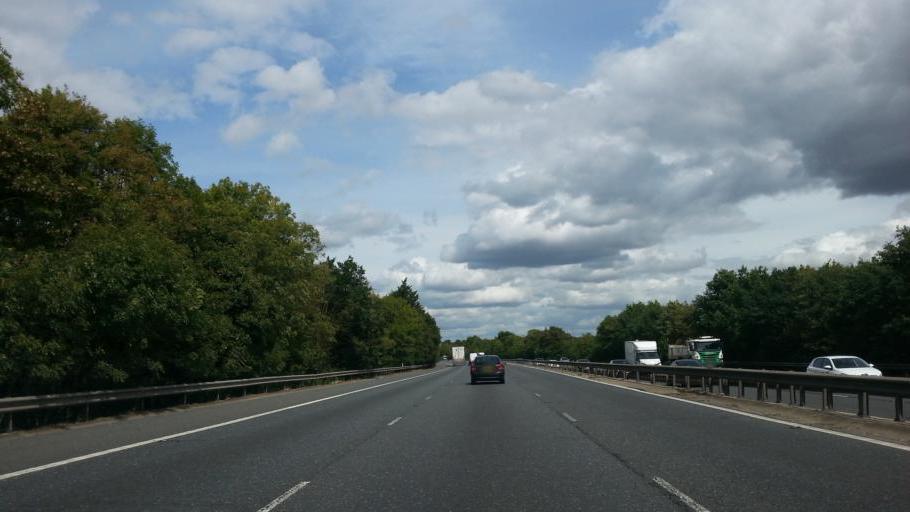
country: GB
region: England
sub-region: Essex
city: Little Hallingbury
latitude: 51.8281
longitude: 0.1890
